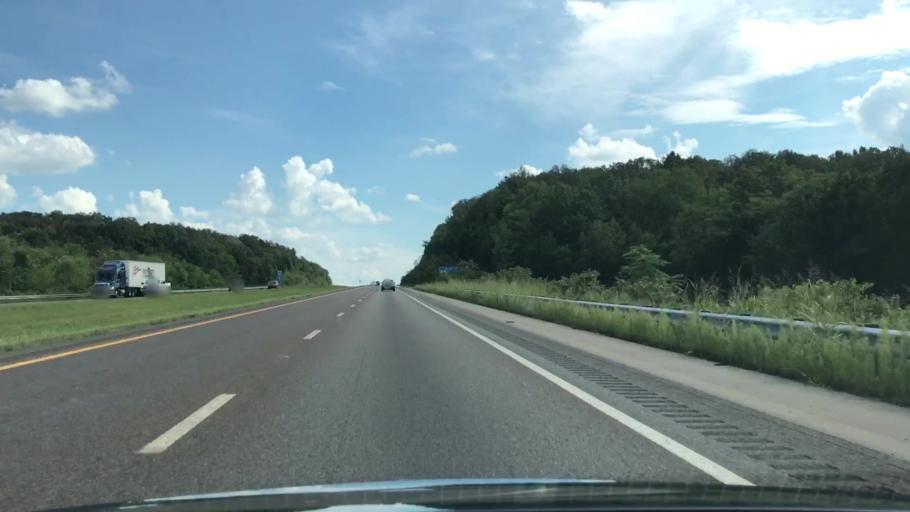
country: US
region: Tennessee
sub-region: Marshall County
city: Lewisburg
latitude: 35.5409
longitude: -86.9054
